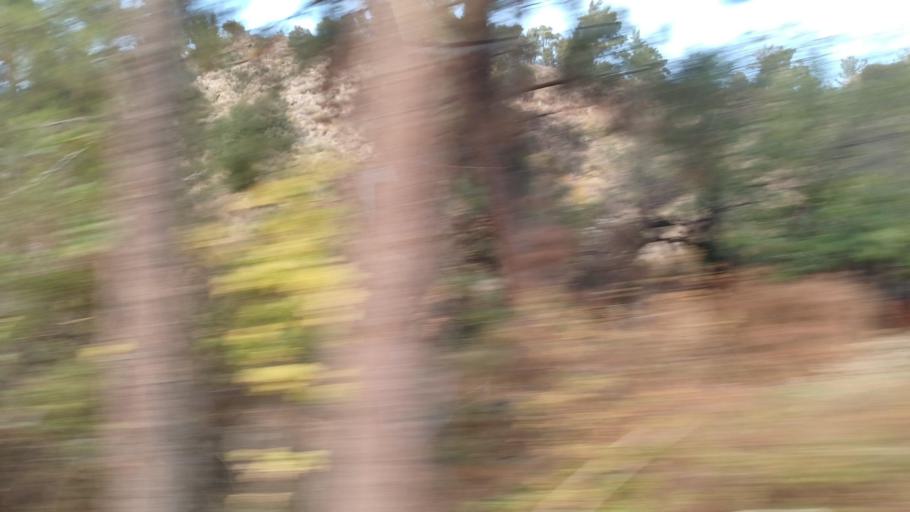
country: CY
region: Lefkosia
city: Kakopetria
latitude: 34.9780
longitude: 32.9093
